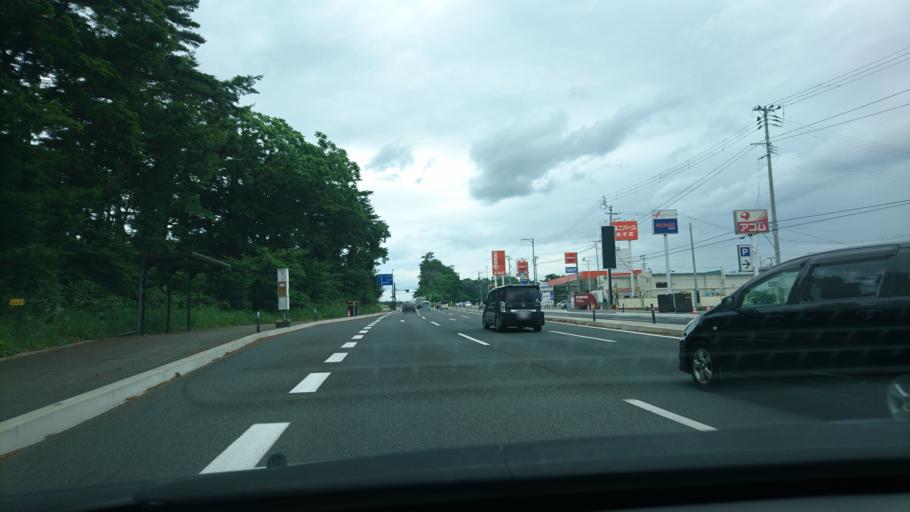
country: JP
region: Iwate
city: Morioka-shi
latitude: 39.7729
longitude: 141.1284
